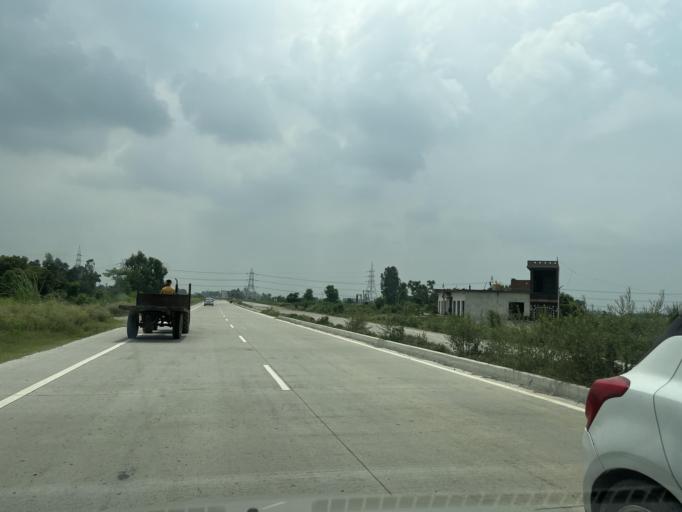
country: IN
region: Uttar Pradesh
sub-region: Bijnor
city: Najibabad
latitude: 29.5697
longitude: 78.3389
